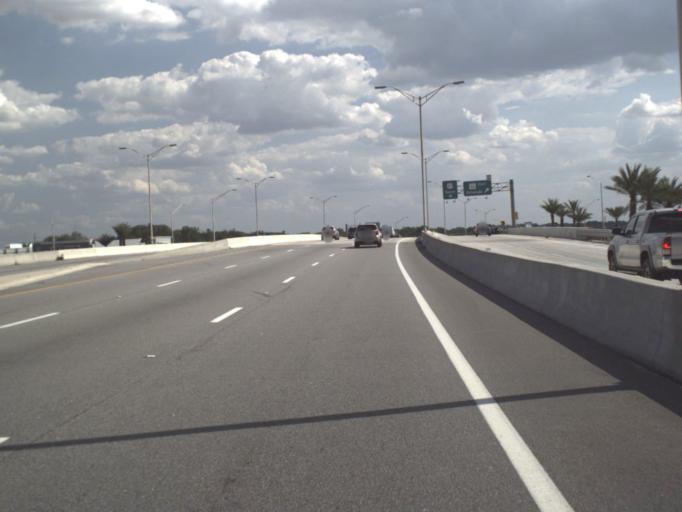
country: US
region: Florida
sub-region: Lake County
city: Minneola
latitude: 28.5483
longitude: -81.7420
